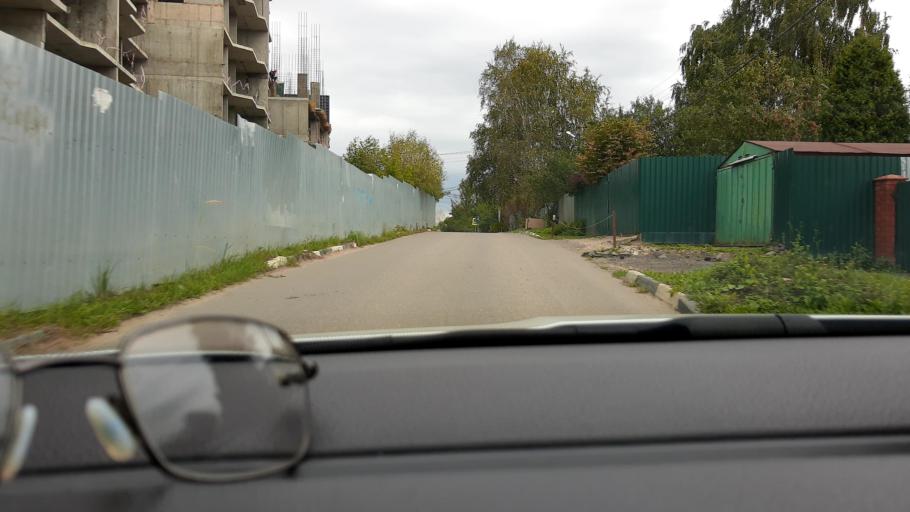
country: RU
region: Moscow
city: Vnukovo
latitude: 55.5948
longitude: 37.2005
